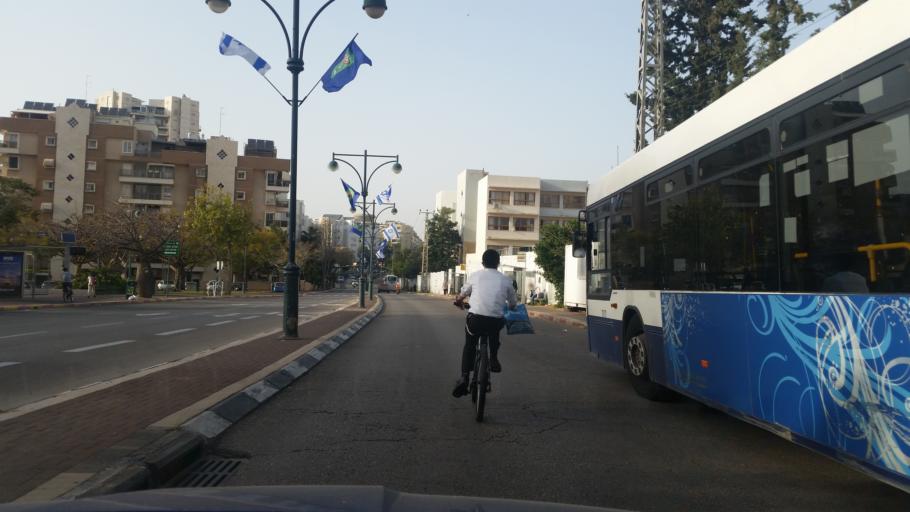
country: IL
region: Tel Aviv
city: Bene Beraq
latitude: 32.0729
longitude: 34.8331
